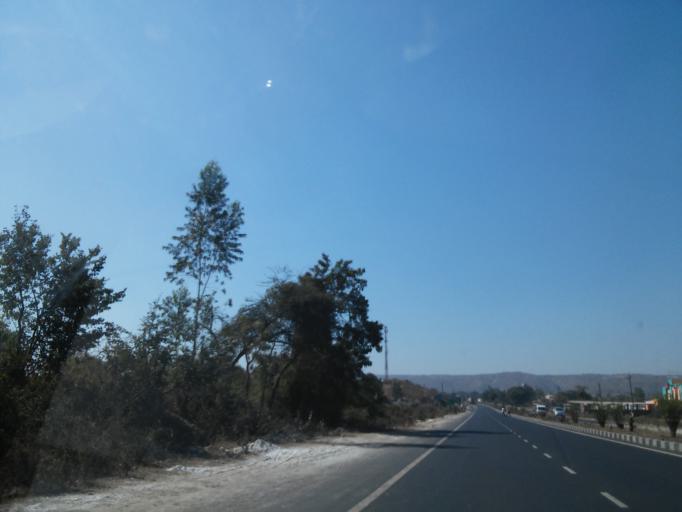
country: IN
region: Gujarat
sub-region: Sabar Kantha
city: Meghraj
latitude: 23.7309
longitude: 73.4104
